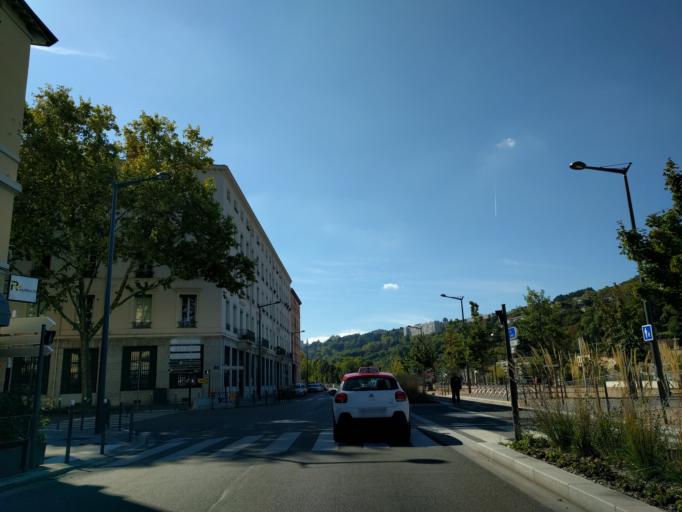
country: FR
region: Rhone-Alpes
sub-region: Departement du Rhone
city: Sainte-Foy-les-Lyon
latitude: 45.7487
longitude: 4.8202
